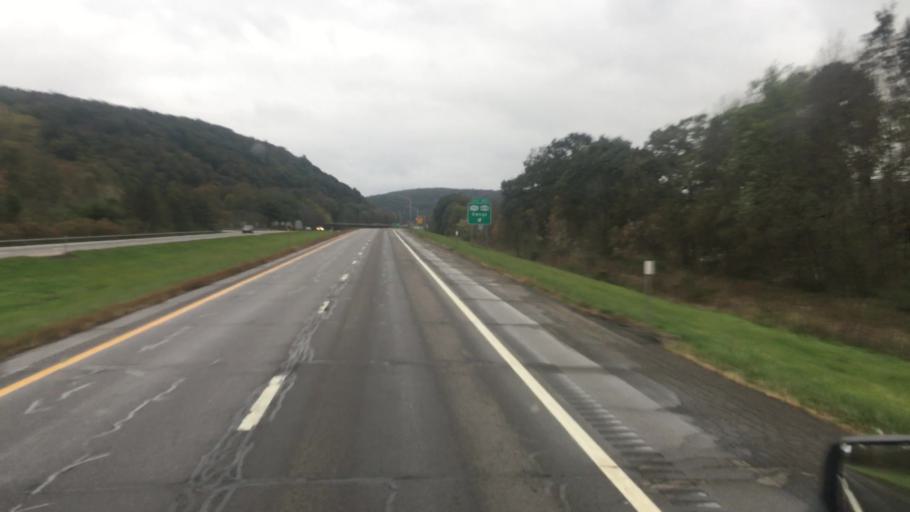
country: US
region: New York
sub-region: Tioga County
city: Owego
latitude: 42.0859
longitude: -76.2249
